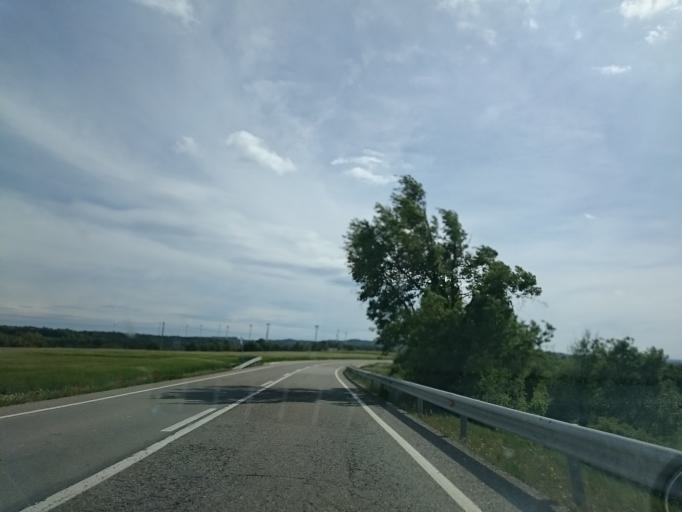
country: ES
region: Catalonia
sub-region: Provincia de Tarragona
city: Santa Coloma de Queralt
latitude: 41.5907
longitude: 1.3959
